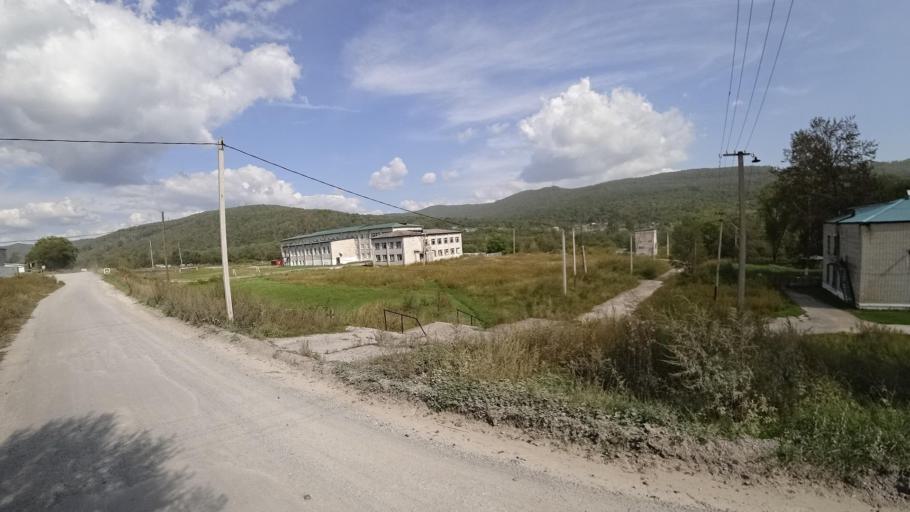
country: RU
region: Jewish Autonomous Oblast
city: Londoko
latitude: 49.0258
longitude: 131.9246
